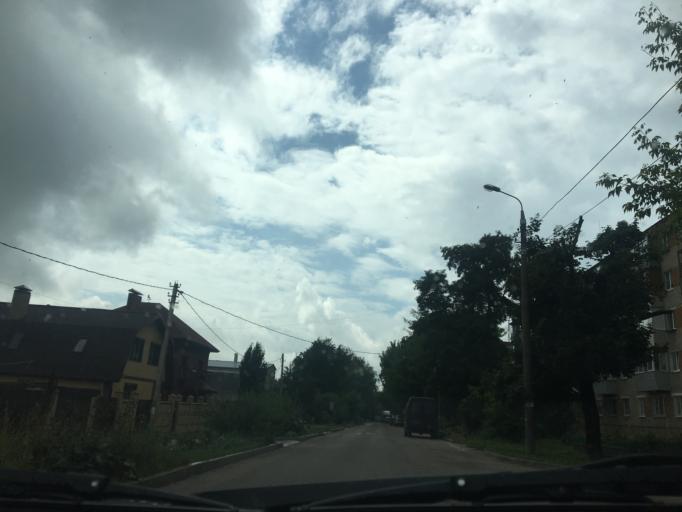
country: RU
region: Tula
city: Mendeleyevskiy
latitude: 54.1532
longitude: 37.5920
